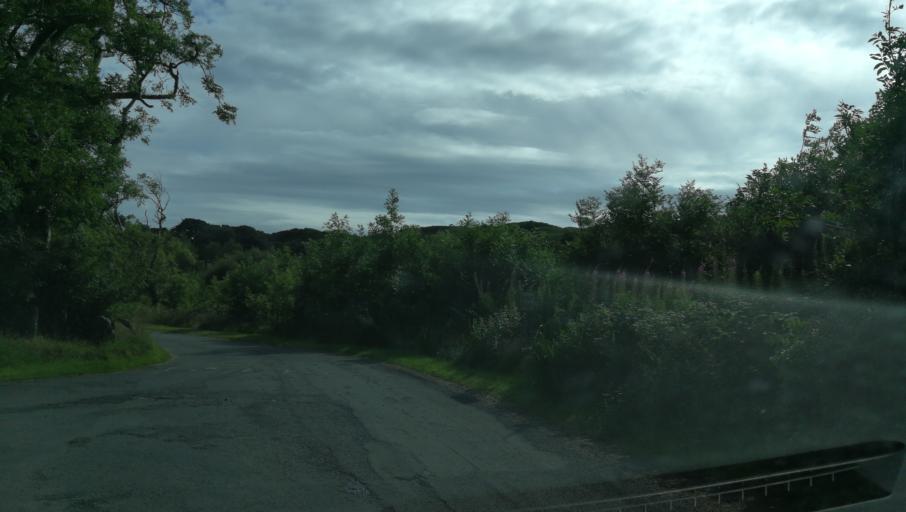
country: GB
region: Scotland
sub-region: Highland
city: Isle of Skye
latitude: 57.3983
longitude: -6.5680
